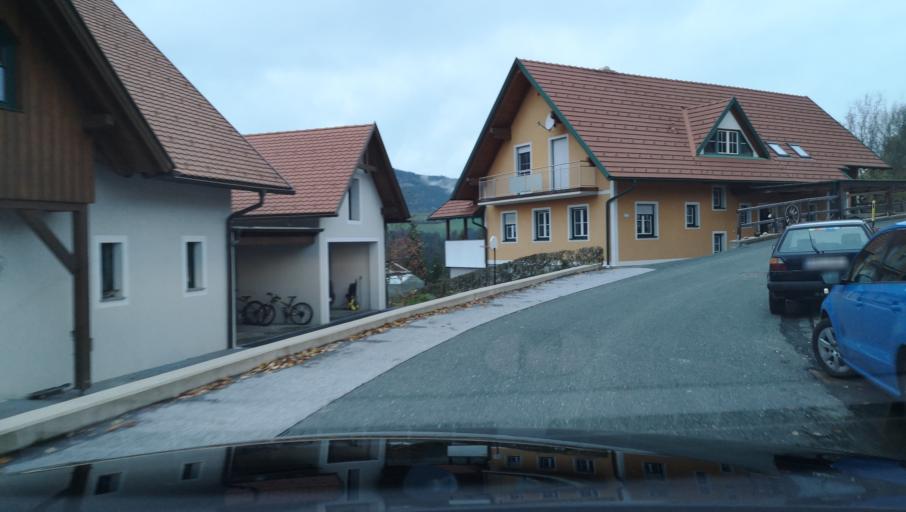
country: AT
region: Styria
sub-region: Politischer Bezirk Weiz
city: Birkfeld
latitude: 47.3490
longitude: 15.6838
